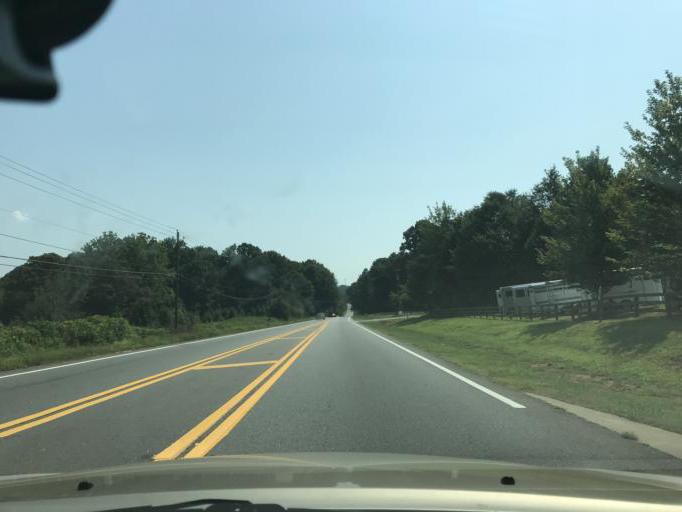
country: US
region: Georgia
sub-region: Hall County
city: Flowery Branch
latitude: 34.2476
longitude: -84.0174
